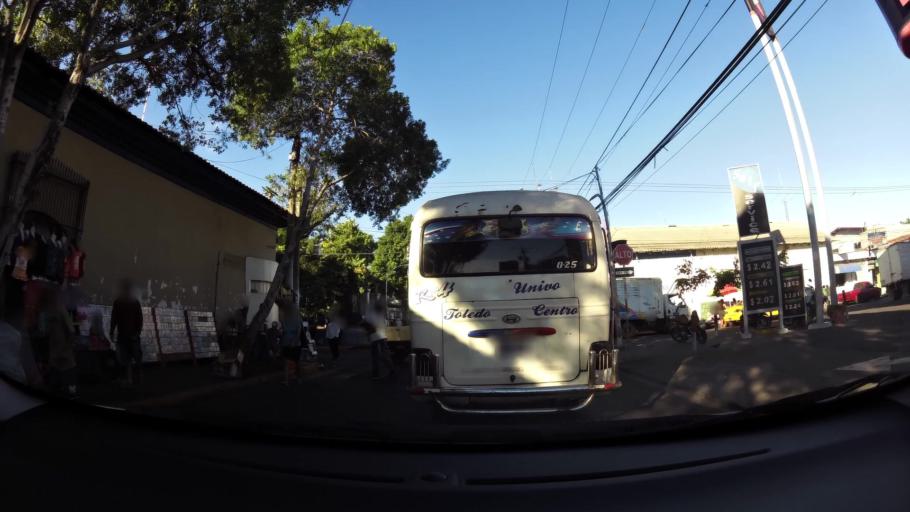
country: SV
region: San Miguel
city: San Miguel
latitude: 13.4830
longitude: -88.1790
